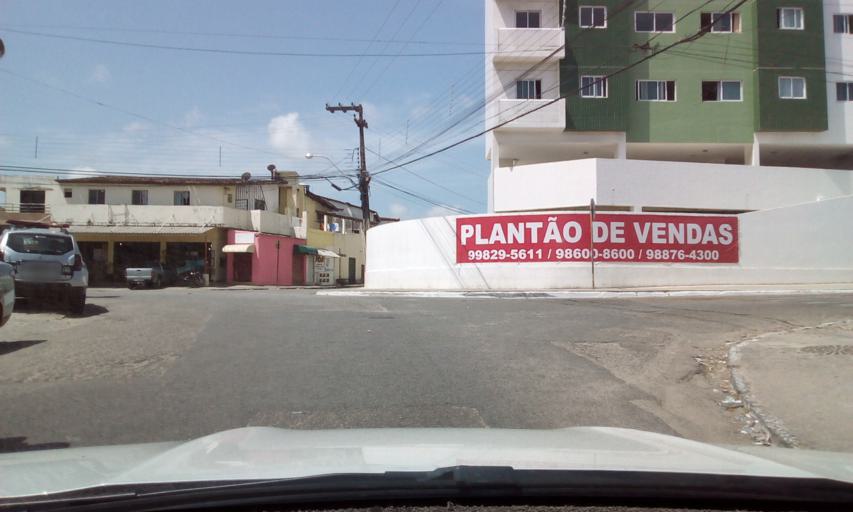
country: BR
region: Paraiba
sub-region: Joao Pessoa
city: Joao Pessoa
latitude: -7.0987
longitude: -34.8660
